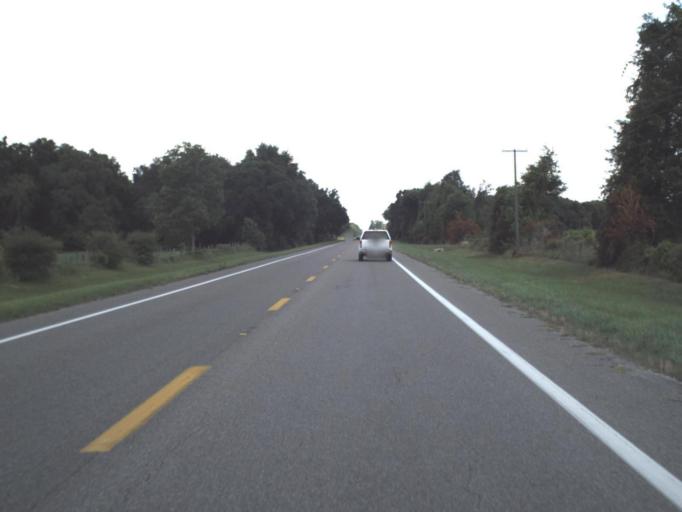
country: US
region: Florida
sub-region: Lafayette County
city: Mayo
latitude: 29.9937
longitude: -83.0116
